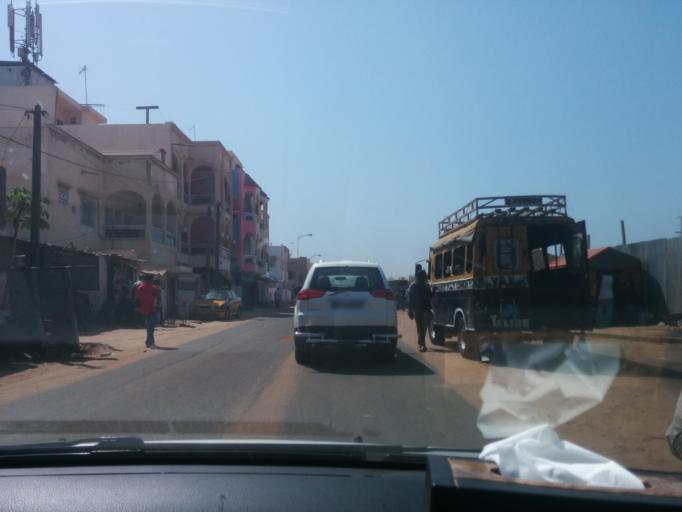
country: SN
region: Dakar
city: Grand Dakar
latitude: 14.7589
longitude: -17.4518
